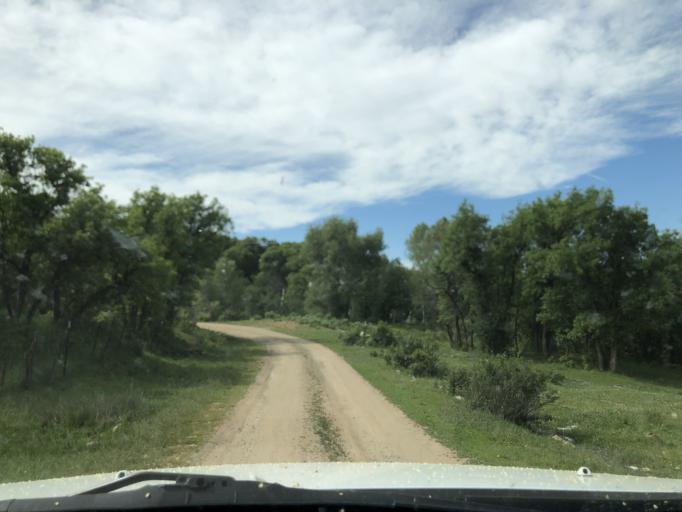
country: US
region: Colorado
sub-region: Delta County
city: Paonia
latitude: 39.0096
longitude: -107.3414
